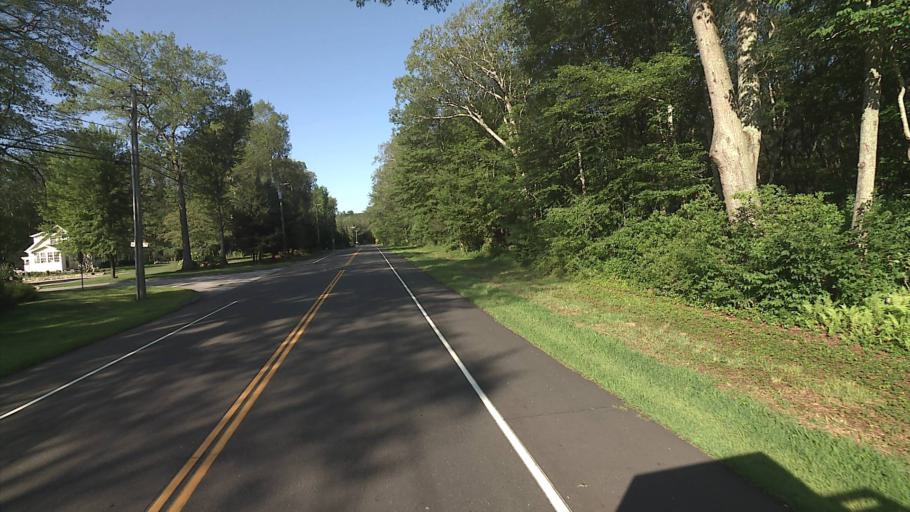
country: US
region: Connecticut
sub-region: New London County
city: Niantic
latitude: 41.3440
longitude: -72.2622
